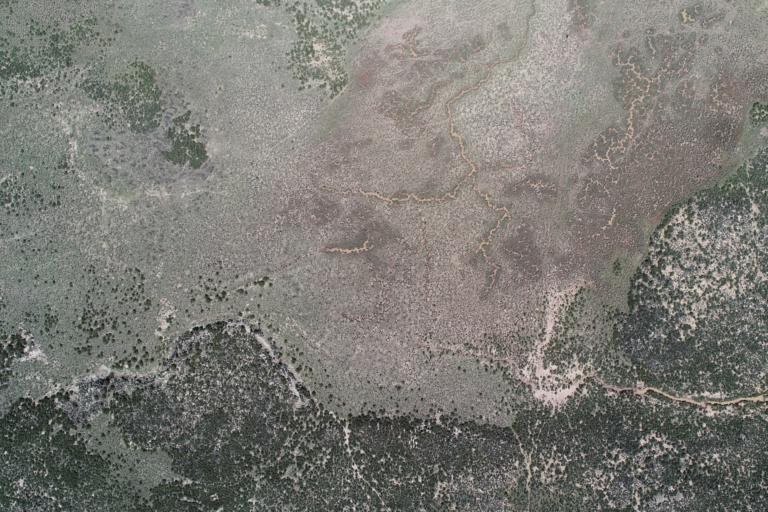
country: BO
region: La Paz
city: Patacamaya
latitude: -17.2910
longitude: -68.4895
